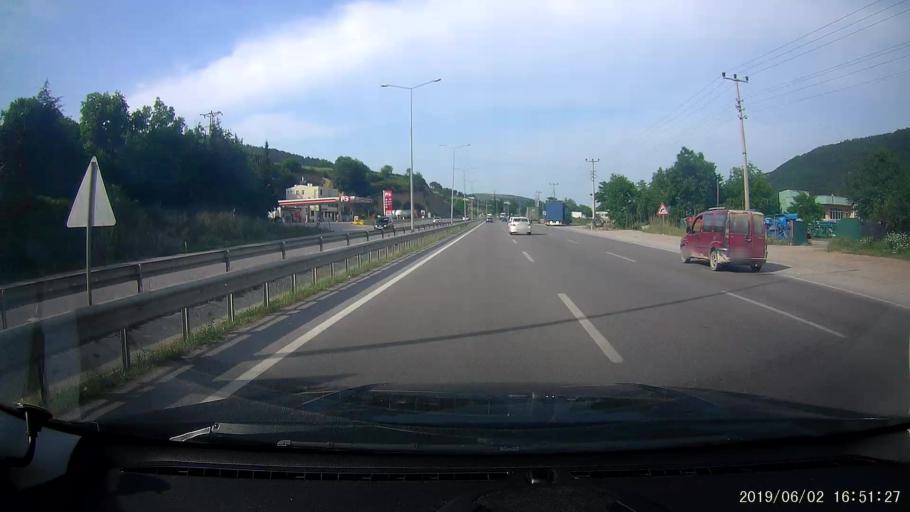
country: TR
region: Samsun
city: Taflan
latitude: 41.2740
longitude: 36.1825
